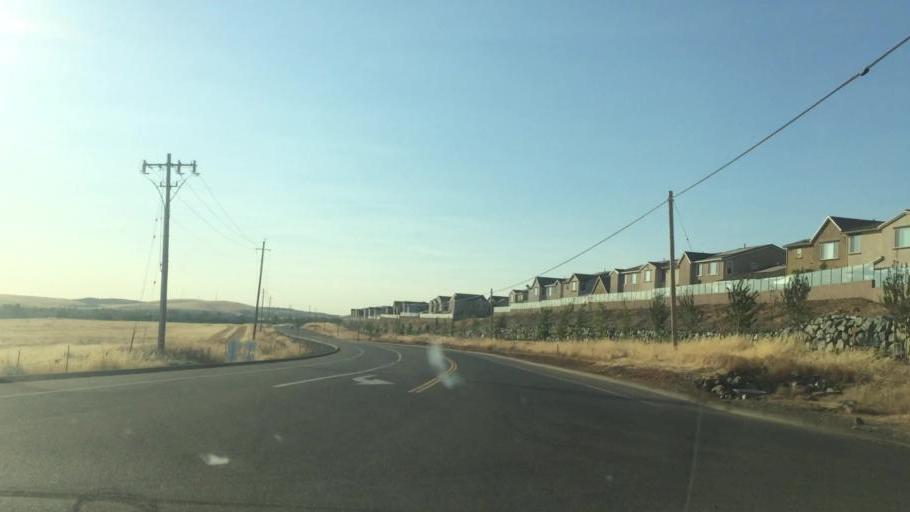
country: US
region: California
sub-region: El Dorado County
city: Cameron Park
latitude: 38.6140
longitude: -121.0455
